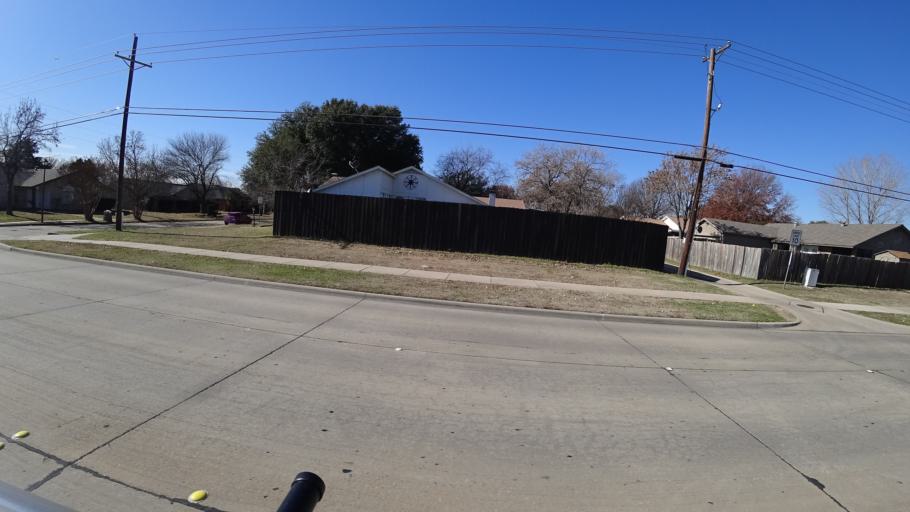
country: US
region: Texas
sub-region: Denton County
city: Lewisville
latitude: 33.0285
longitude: -97.0105
